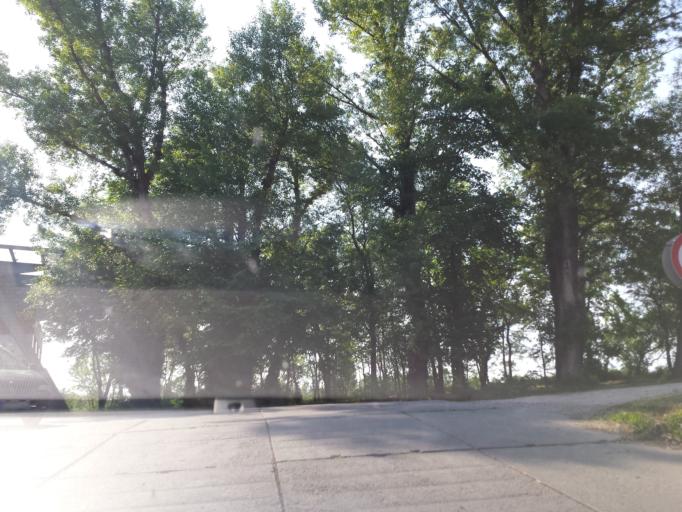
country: AT
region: Lower Austria
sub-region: Politischer Bezirk Ganserndorf
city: Angern an der March
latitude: 48.3825
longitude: 16.8333
